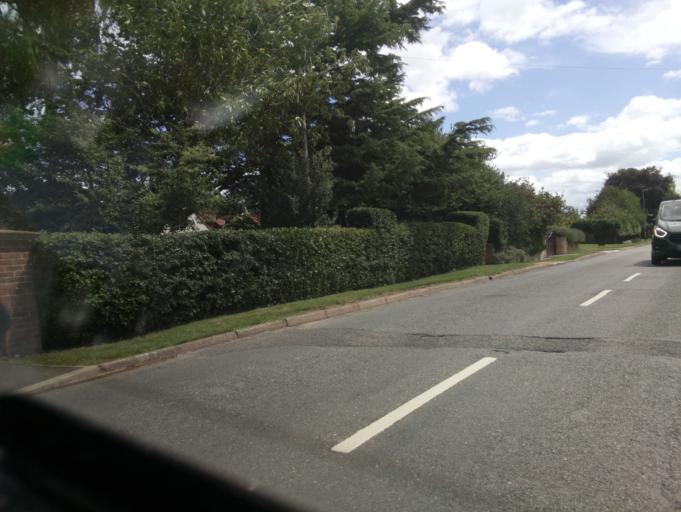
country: GB
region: England
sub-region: Nottinghamshire
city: Cotgrave
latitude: 52.8736
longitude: -1.0744
